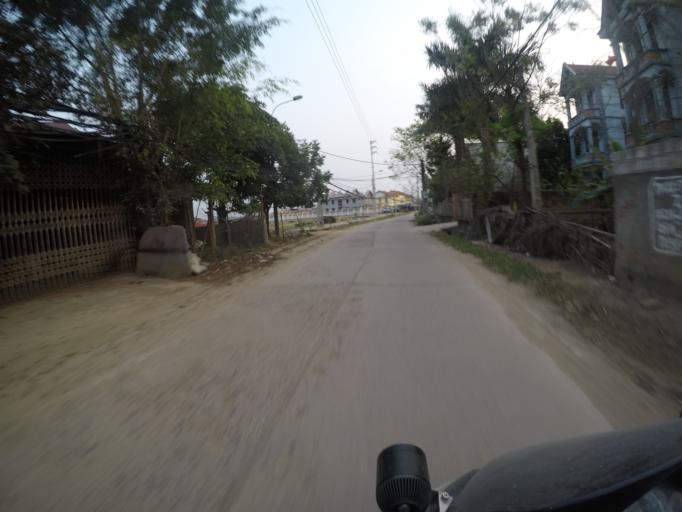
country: VN
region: Vinh Phuc
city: Trai Ngau
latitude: 21.4609
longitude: 105.5697
